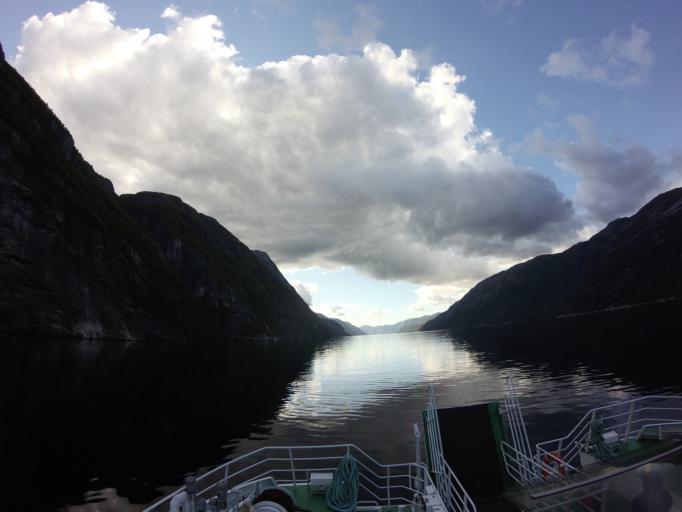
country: NO
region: Rogaland
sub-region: Hjelmeland
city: Hjelmelandsvagen
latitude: 59.0326
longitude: 6.5197
